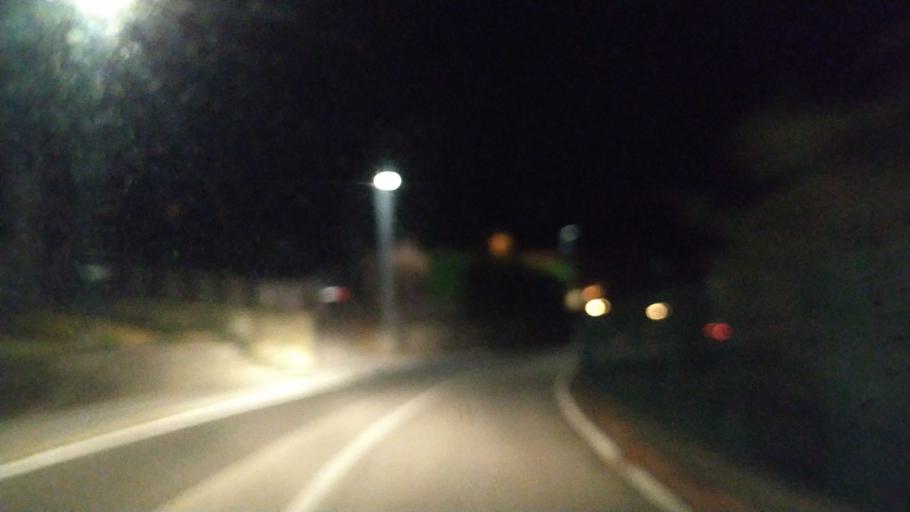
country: IT
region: Piedmont
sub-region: Provincia di Biella
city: Occhieppo Superiore
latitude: 45.5689
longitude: 8.0016
